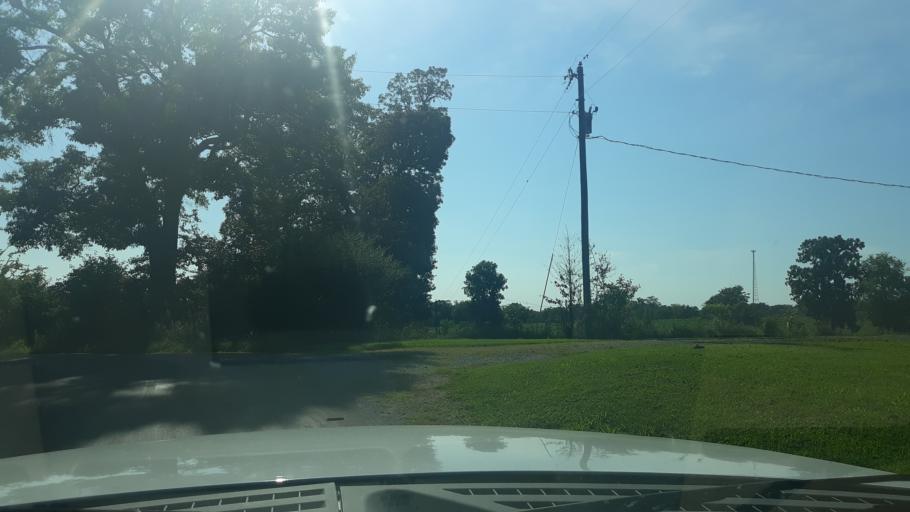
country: US
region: Illinois
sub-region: Saline County
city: Harrisburg
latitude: 37.8524
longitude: -88.5990
